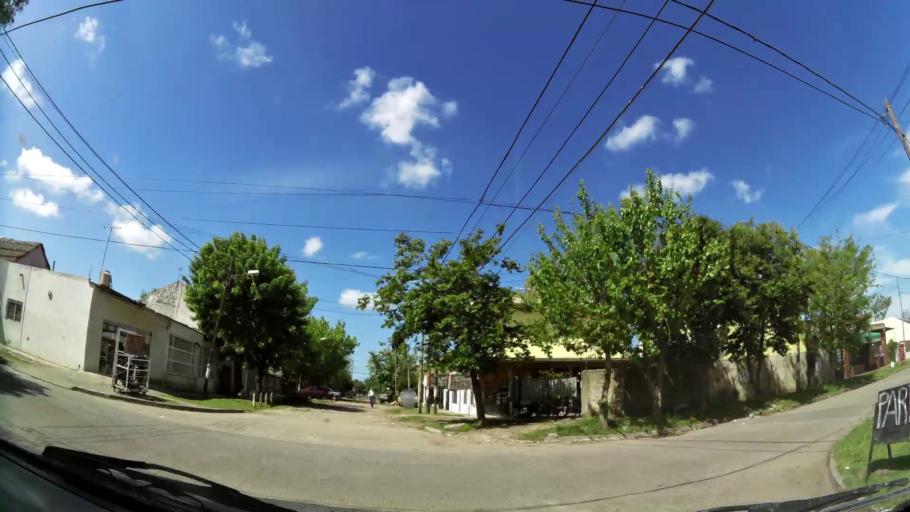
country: AR
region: Buenos Aires
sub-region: Partido de Quilmes
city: Quilmes
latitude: -34.8231
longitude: -58.2725
